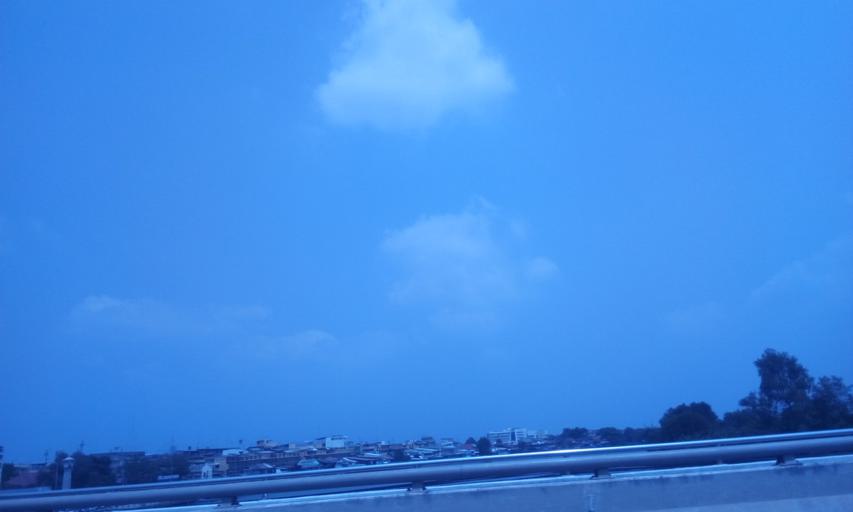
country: TH
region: Chachoengsao
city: Chachoengsao
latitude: 13.6881
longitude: 101.0771
